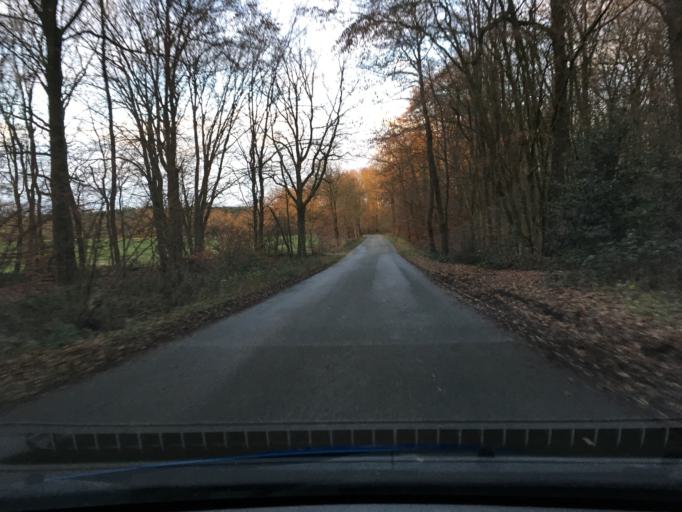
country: DE
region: Lower Saxony
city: Amelinghausen
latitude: 53.1378
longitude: 10.2038
